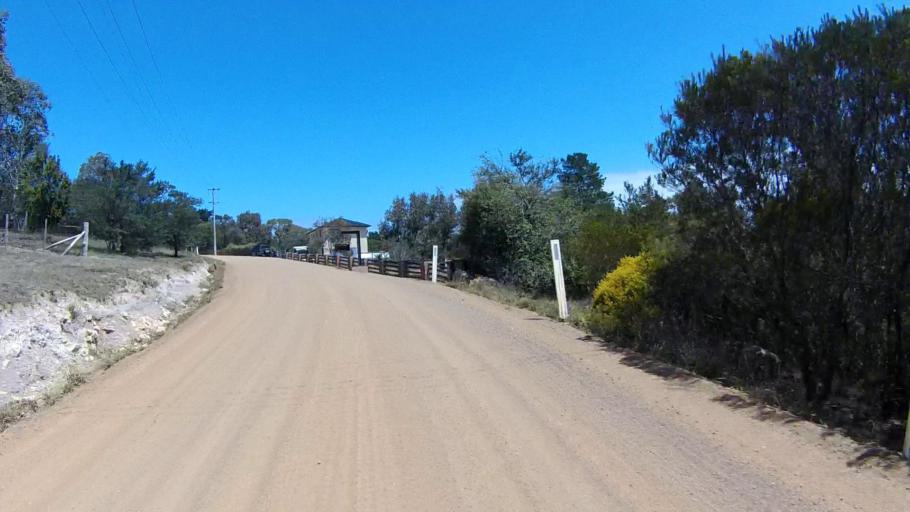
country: AU
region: Tasmania
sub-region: Clarence
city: Lauderdale
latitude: -42.9368
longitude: 147.4609
